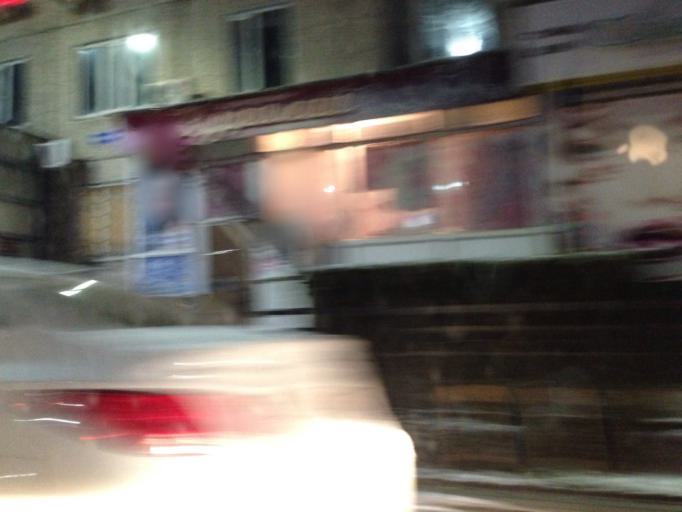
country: KZ
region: Astana Qalasy
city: Astana
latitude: 51.1818
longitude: 71.4171
